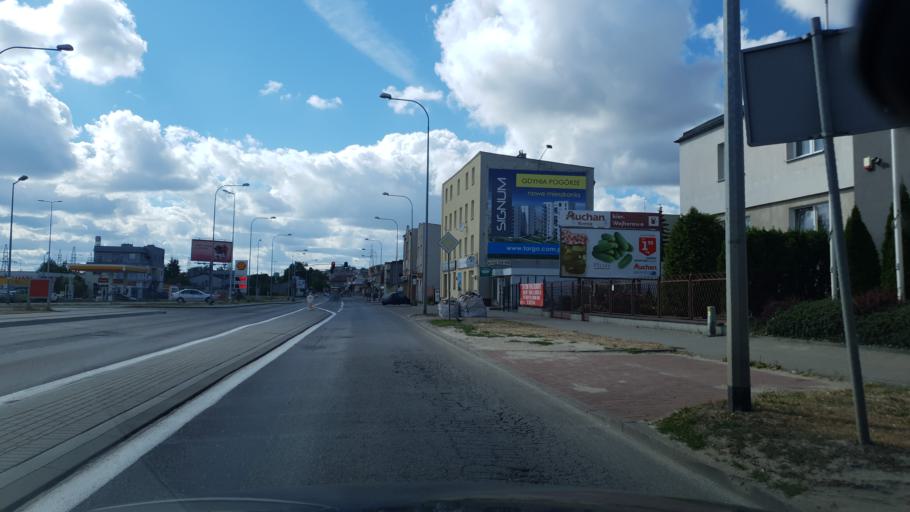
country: PL
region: Pomeranian Voivodeship
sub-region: Gdynia
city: Gdynia
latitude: 54.5491
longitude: 18.5148
